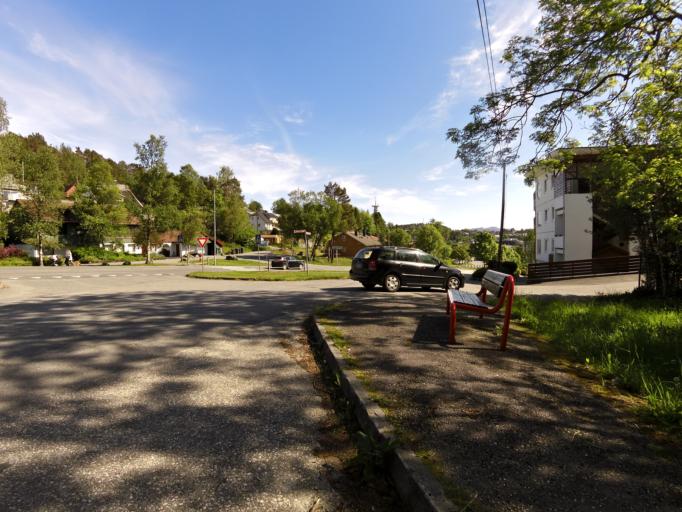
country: NO
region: Hordaland
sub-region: Stord
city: Leirvik
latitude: 59.7850
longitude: 5.4984
